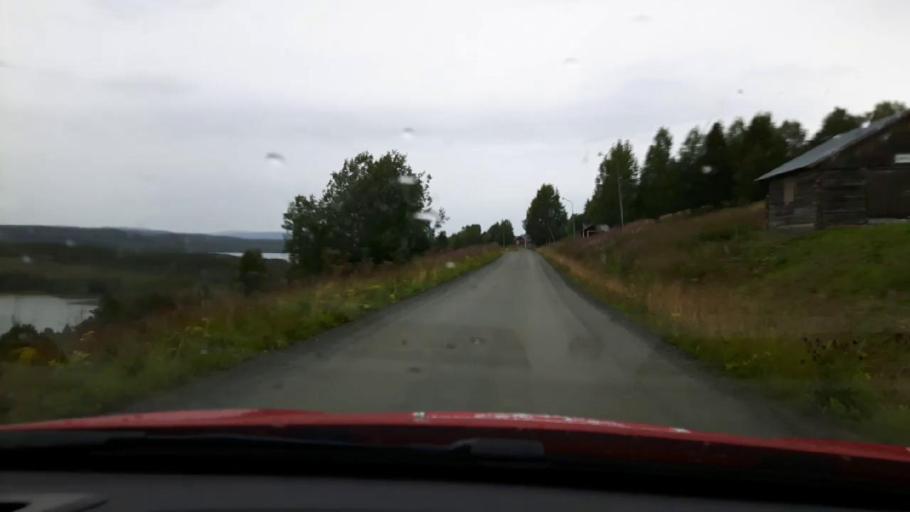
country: SE
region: Jaemtland
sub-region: Are Kommun
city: Are
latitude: 63.4658
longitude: 12.8139
